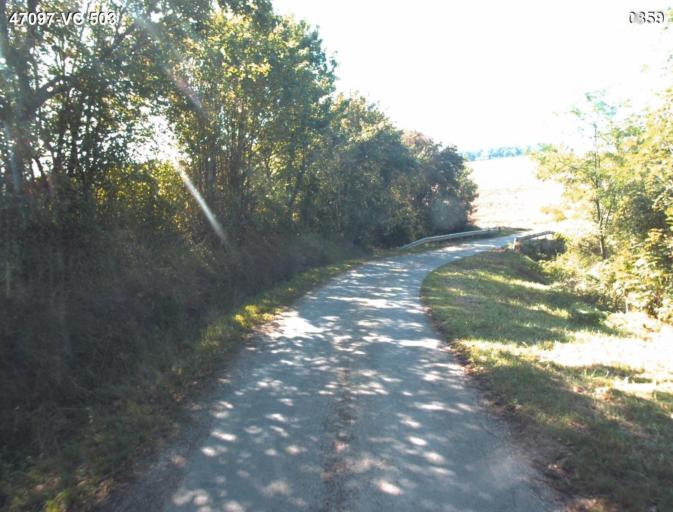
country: FR
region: Aquitaine
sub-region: Departement du Lot-et-Garonne
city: Vianne
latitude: 44.1995
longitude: 0.3701
